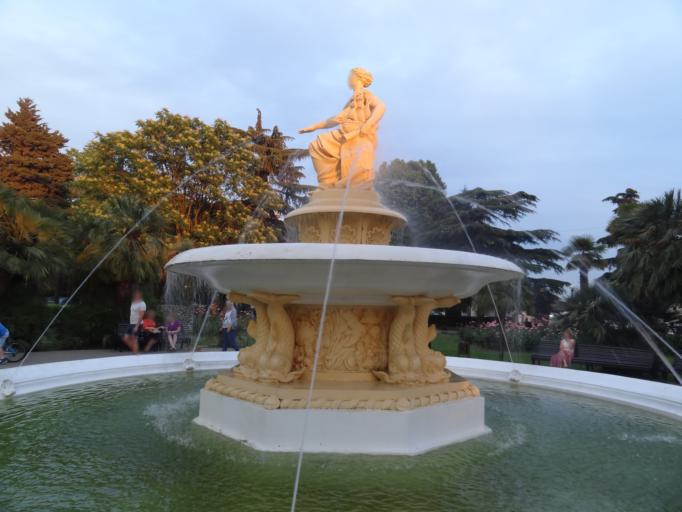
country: RU
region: Krasnodarskiy
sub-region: Sochi City
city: Sochi
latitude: 43.5811
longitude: 39.7192
